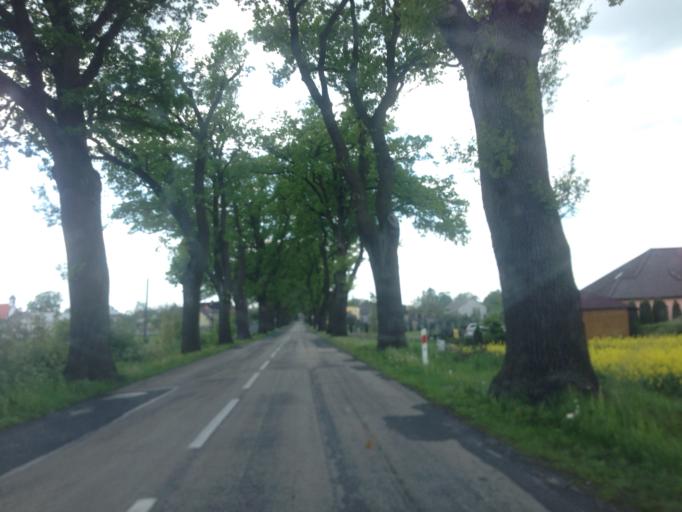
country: PL
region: Kujawsko-Pomorskie
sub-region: Powiat swiecki
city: Pruszcz
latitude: 53.2847
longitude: 18.1328
